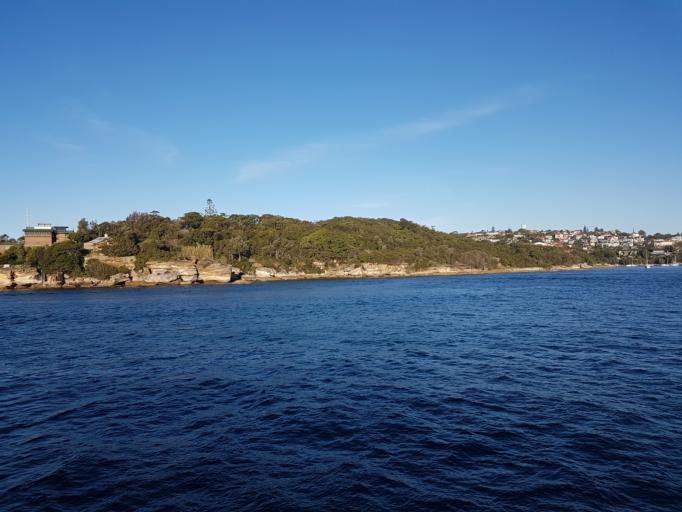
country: AU
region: New South Wales
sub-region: Woollahra
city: Point Piper
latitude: -33.8515
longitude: 151.2619
